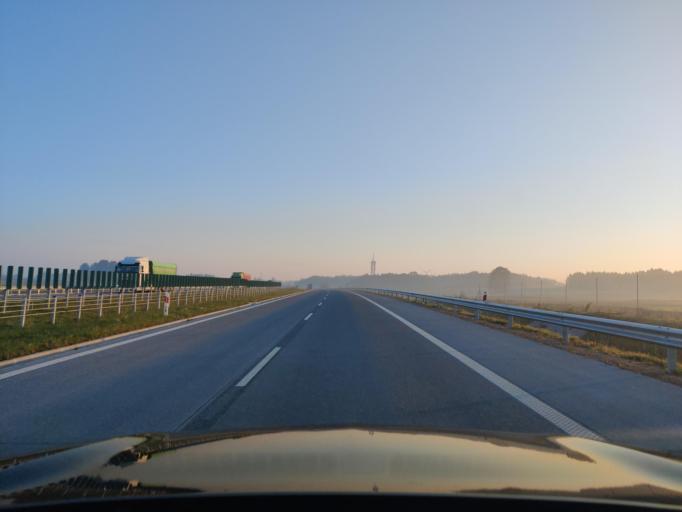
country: PL
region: Masovian Voivodeship
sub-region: Powiat mlawski
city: Mlawa
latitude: 53.0863
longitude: 20.4023
